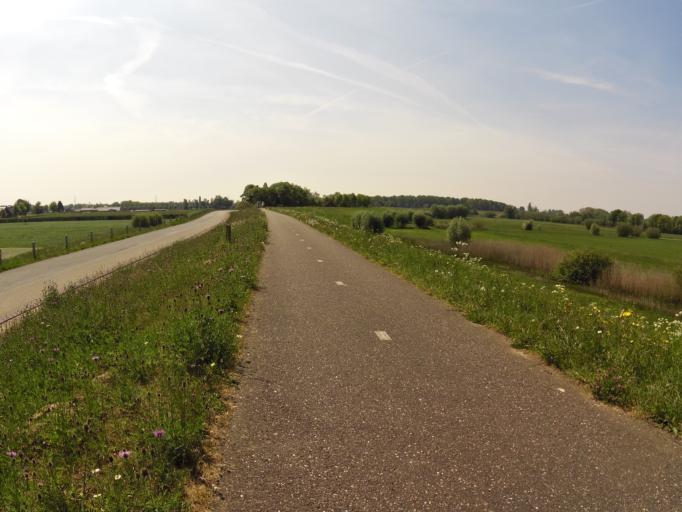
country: NL
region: Gelderland
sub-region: Gemeente Neerijnen
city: Neerijnen
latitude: 51.8052
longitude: 5.3032
